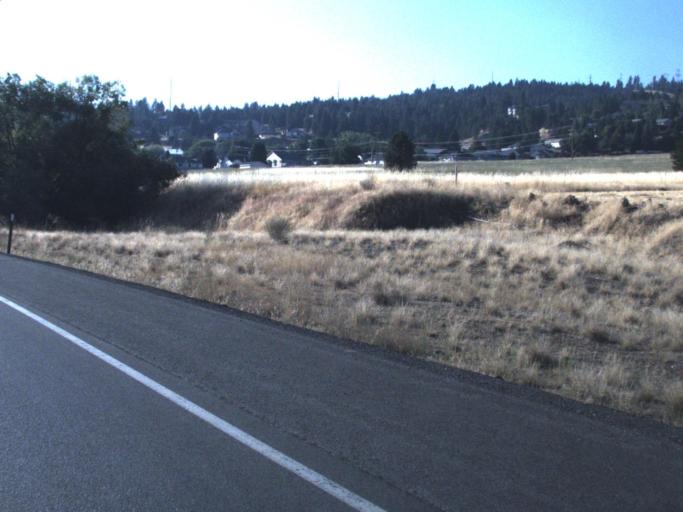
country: US
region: Washington
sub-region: Spokane County
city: Liberty Lake
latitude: 47.7017
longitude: -117.1491
